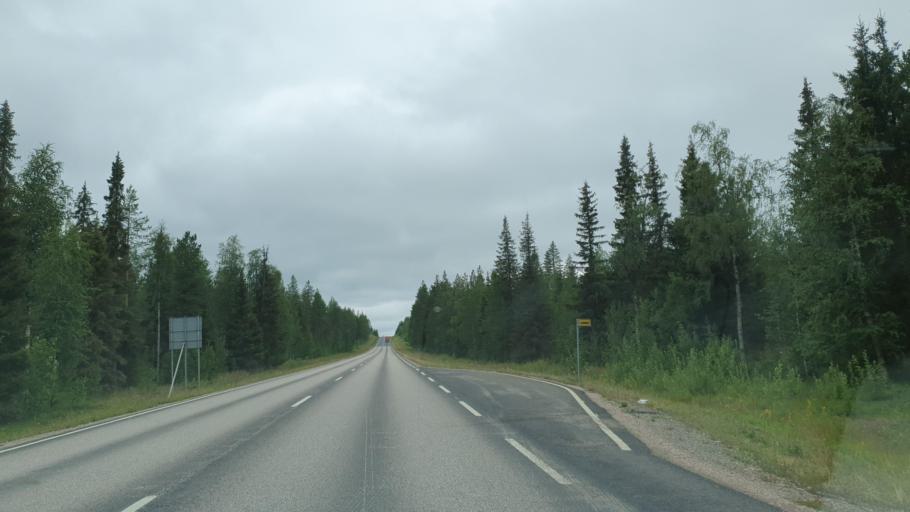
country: FI
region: Lapland
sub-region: Pohjois-Lappi
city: Sodankylae
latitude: 67.4141
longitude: 26.5109
